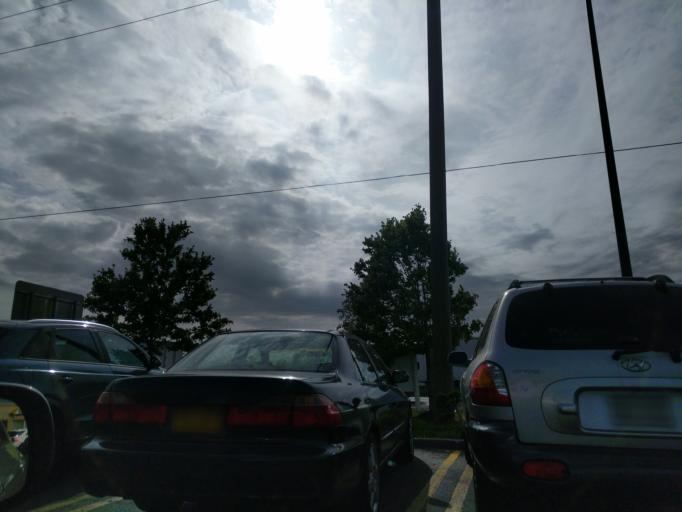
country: US
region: New York
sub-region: Nassau County
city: Inwood
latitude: 40.6267
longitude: -73.7401
